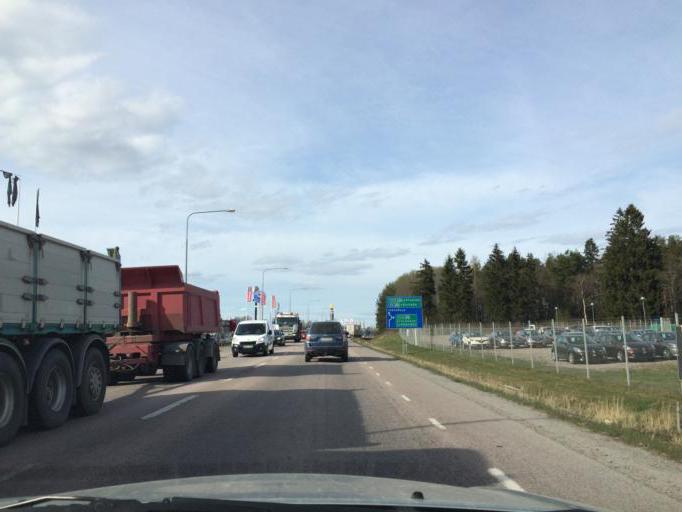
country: SE
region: Soedermanland
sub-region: Eskilstuna Kommun
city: Torshalla
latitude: 59.3891
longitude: 16.4663
